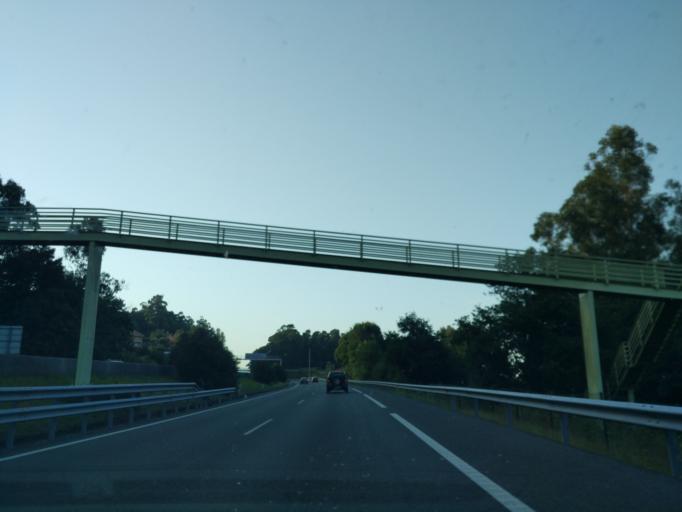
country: ES
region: Galicia
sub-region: Provincia de Pontevedra
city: Pontevedra
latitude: 42.3782
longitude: -8.6362
